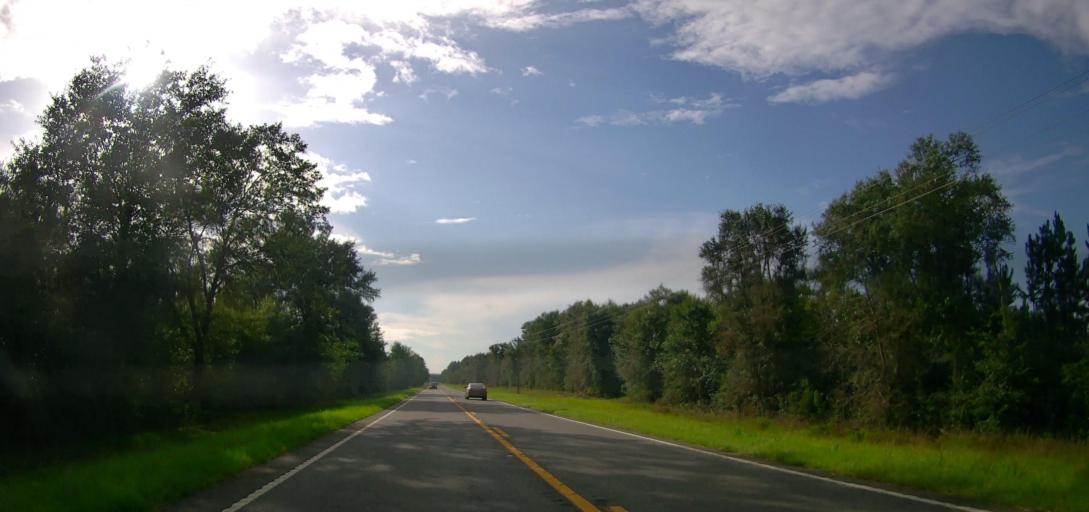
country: US
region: Georgia
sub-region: Coffee County
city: Nicholls
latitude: 31.3345
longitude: -82.5927
